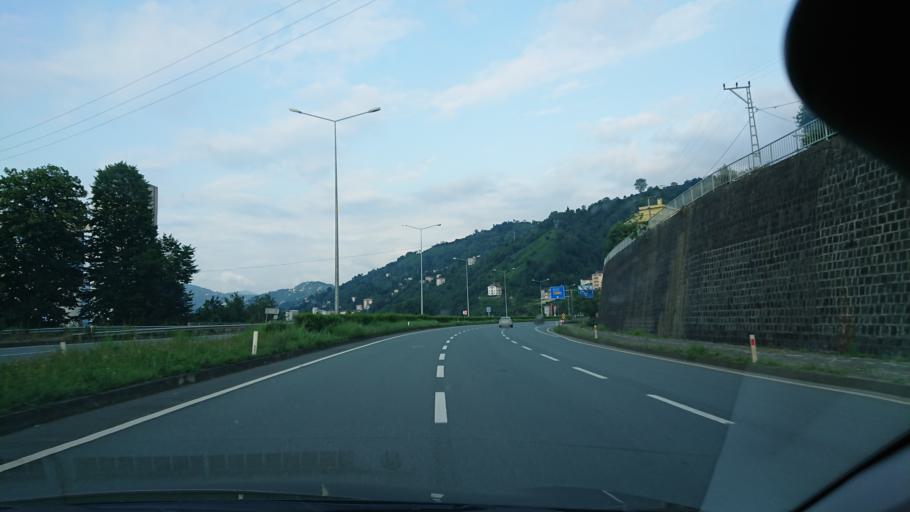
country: TR
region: Rize
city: Cayeli
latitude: 41.0769
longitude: 40.6795
